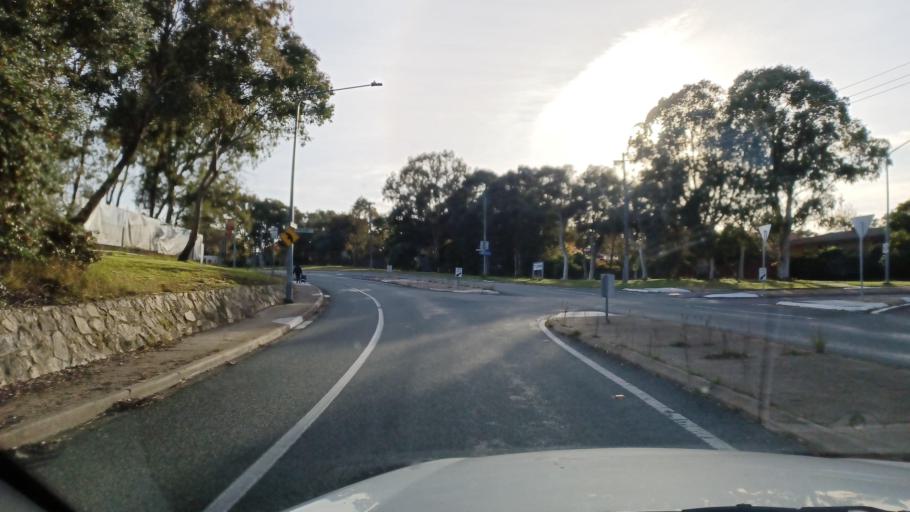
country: AU
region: Australian Capital Territory
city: Belconnen
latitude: -35.1994
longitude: 149.0443
